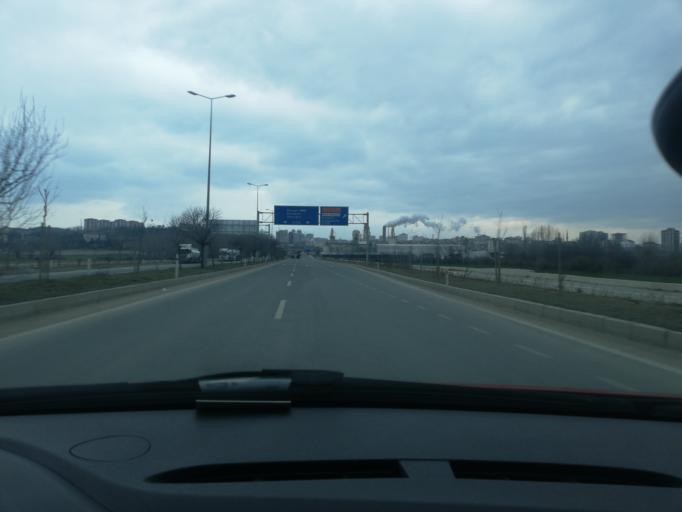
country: TR
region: Kastamonu
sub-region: Cide
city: Kastamonu
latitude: 41.4123
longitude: 33.8042
